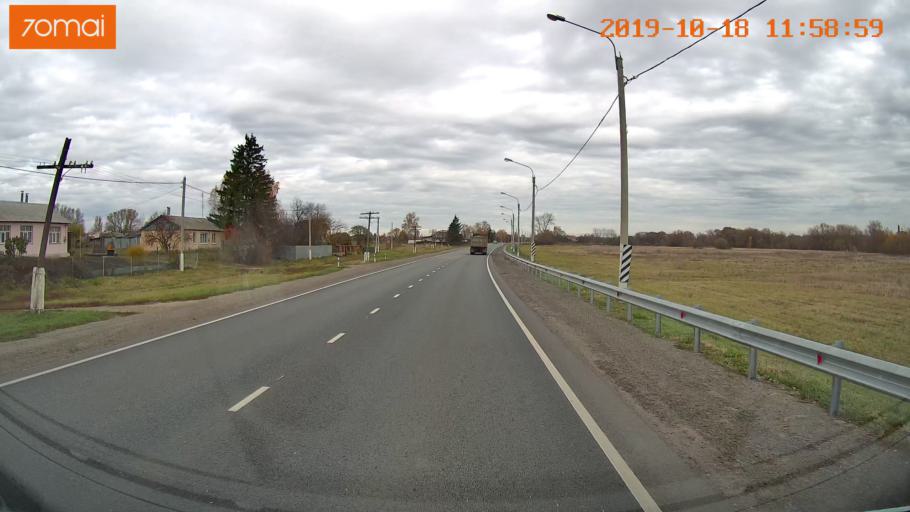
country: RU
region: Rjazan
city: Zakharovo
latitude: 54.2774
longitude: 39.1715
